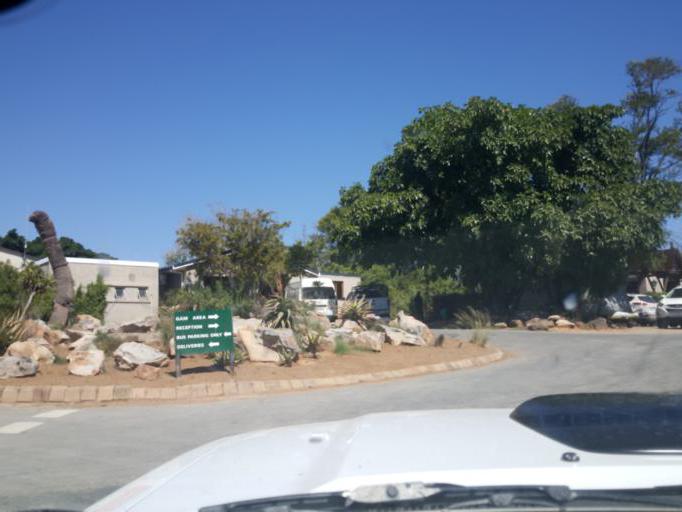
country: ZA
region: Eastern Cape
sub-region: Cacadu District Municipality
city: Kirkwood
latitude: -33.4438
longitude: 25.7456
